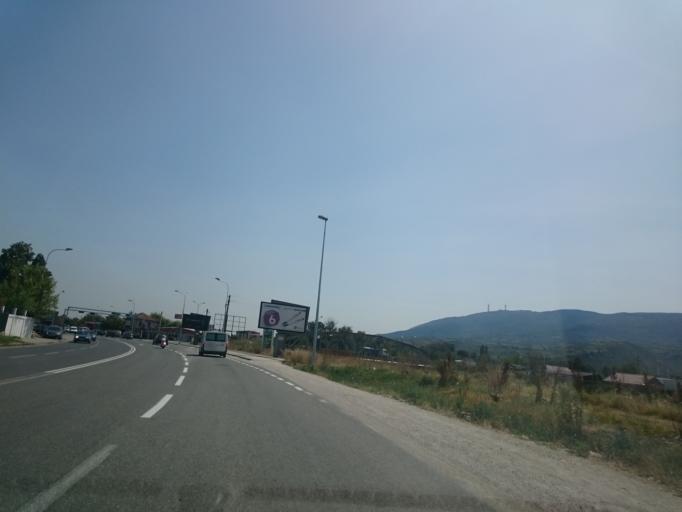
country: MK
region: Saraj
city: Saraj
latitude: 42.0068
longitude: 21.3313
